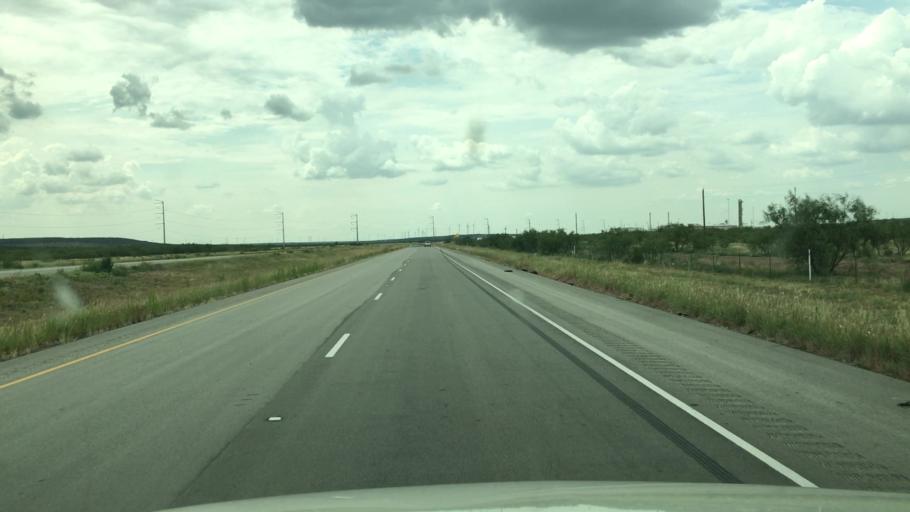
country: US
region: Texas
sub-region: Glasscock County
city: Garden City
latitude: 31.9661
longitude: -101.2302
